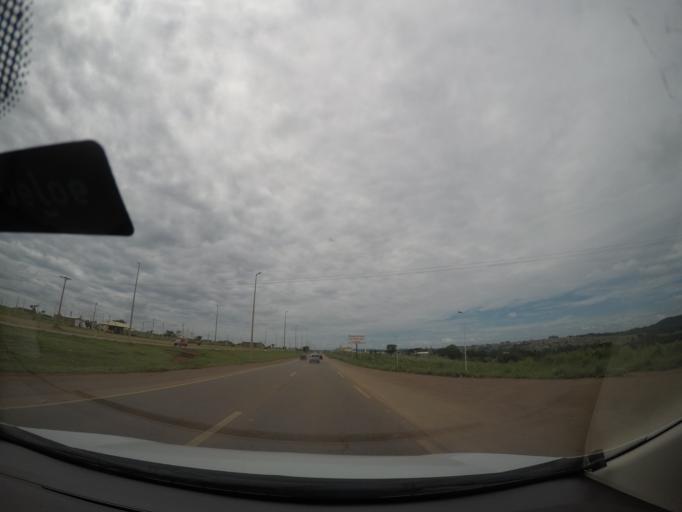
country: BR
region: Goias
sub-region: Goianira
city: Goianira
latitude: -16.5282
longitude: -49.4105
